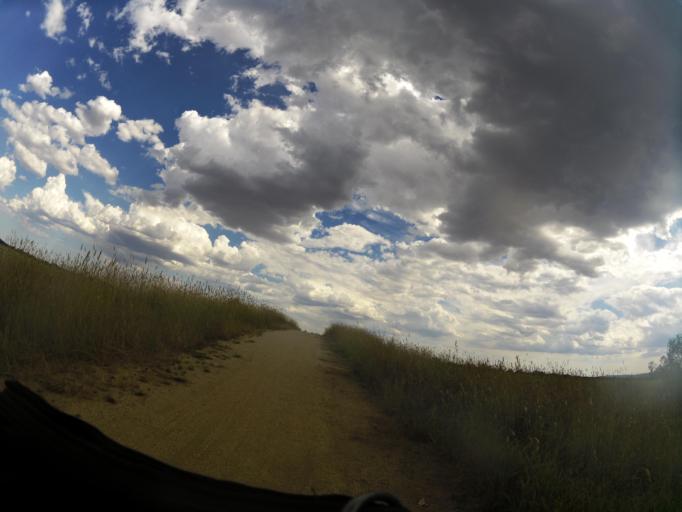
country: AU
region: Victoria
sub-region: Wellington
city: Heyfield
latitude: -37.9999
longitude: 146.6983
